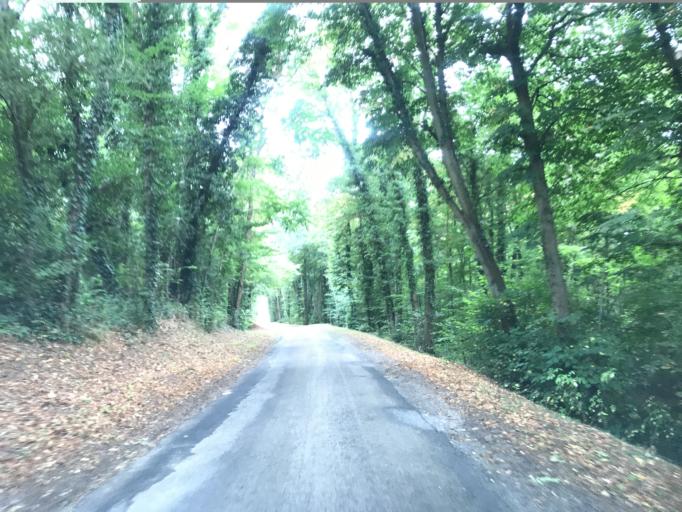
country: FR
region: Haute-Normandie
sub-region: Departement de l'Eure
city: Houlbec-Cocherel
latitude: 49.0620
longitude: 1.3361
